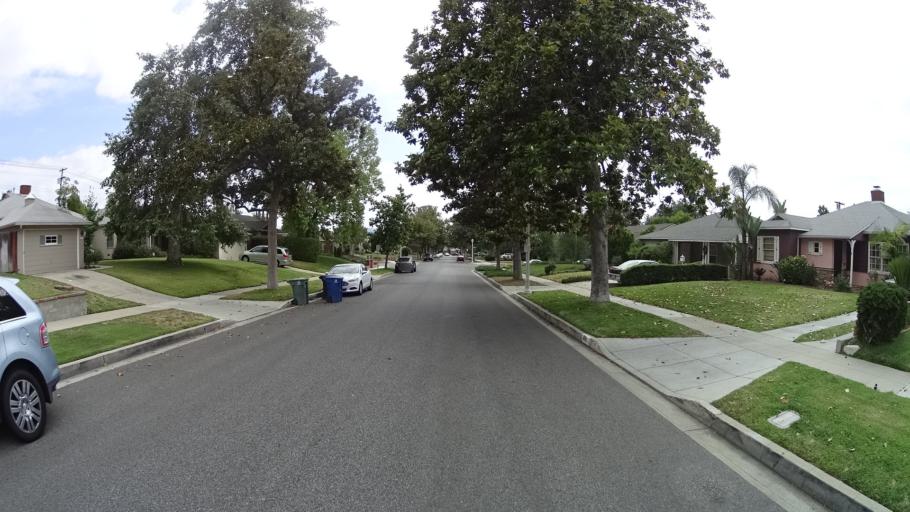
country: US
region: California
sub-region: Los Angeles County
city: Burbank
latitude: 34.1971
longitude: -118.3211
